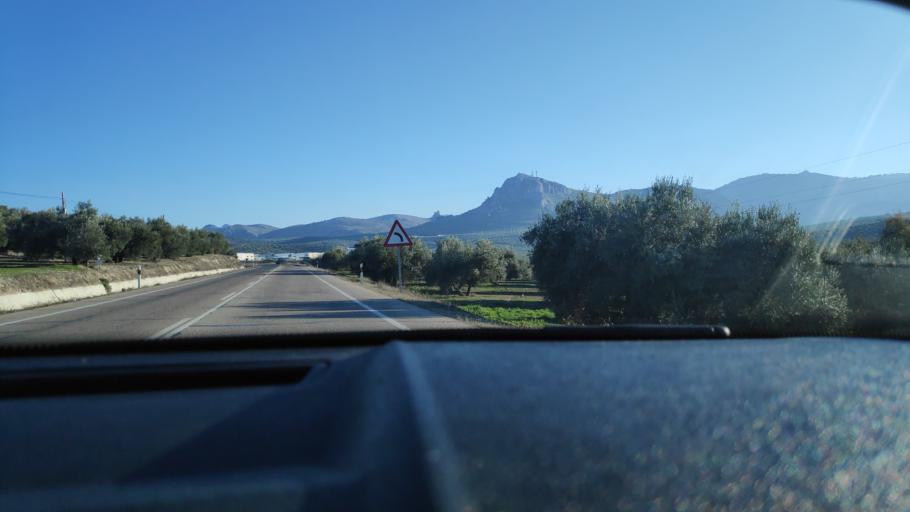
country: ES
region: Andalusia
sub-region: Province of Cordoba
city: Luque
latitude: 37.5855
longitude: -4.2913
